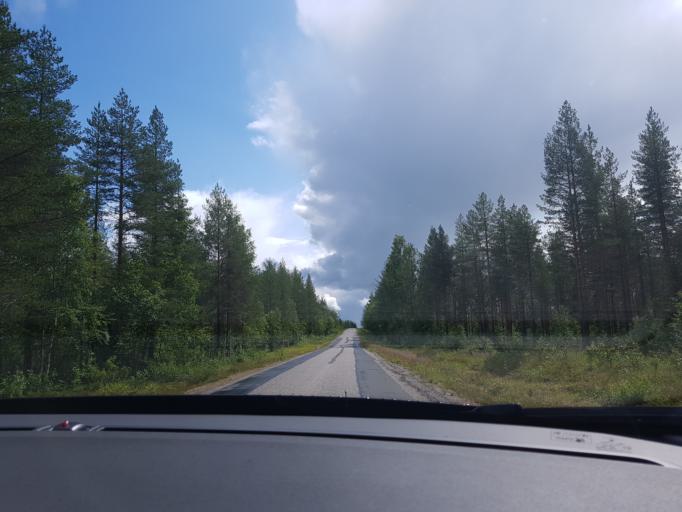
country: FI
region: Kainuu
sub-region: Kehys-Kainuu
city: Kuhmo
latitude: 64.4589
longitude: 29.6398
